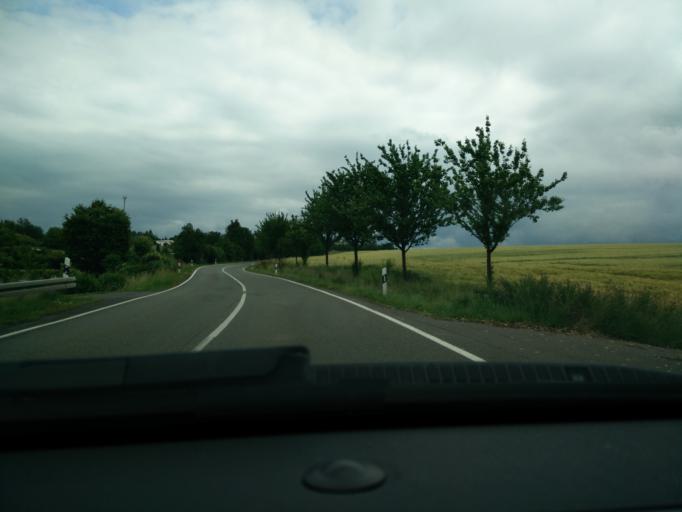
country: DE
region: Saxony
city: Geithain
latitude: 51.0613
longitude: 12.6744
